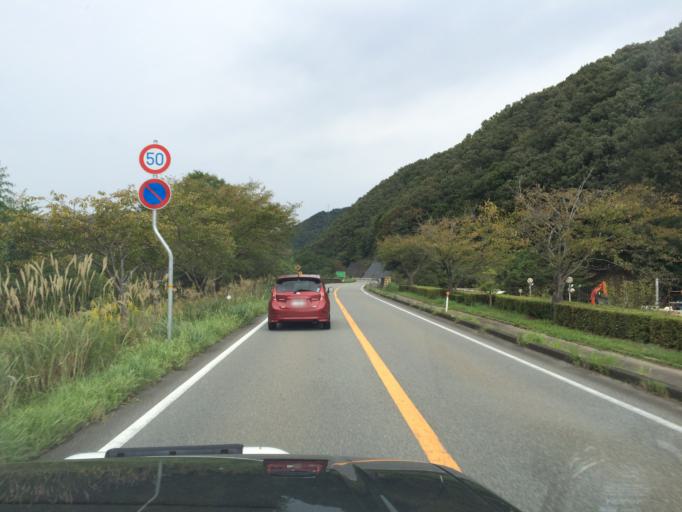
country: JP
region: Hyogo
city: Toyooka
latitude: 35.3604
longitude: 134.8287
